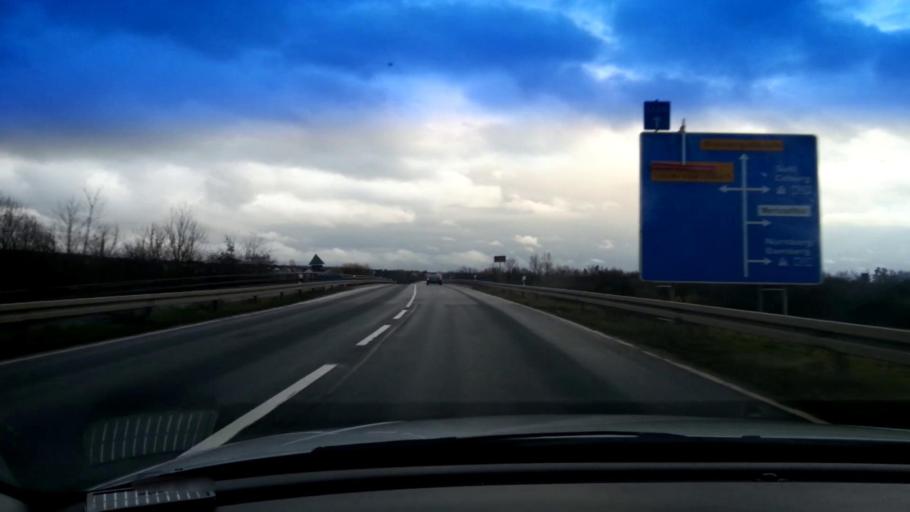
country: DE
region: Bavaria
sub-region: Upper Franconia
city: Breitengussbach
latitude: 49.9825
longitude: 10.8838
